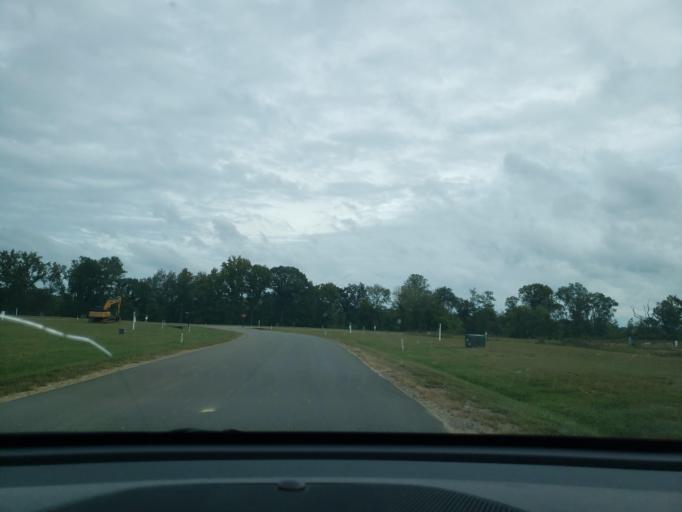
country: US
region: Virginia
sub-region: City of Fredericksburg
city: Fredericksburg
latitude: 38.2468
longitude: -77.3990
